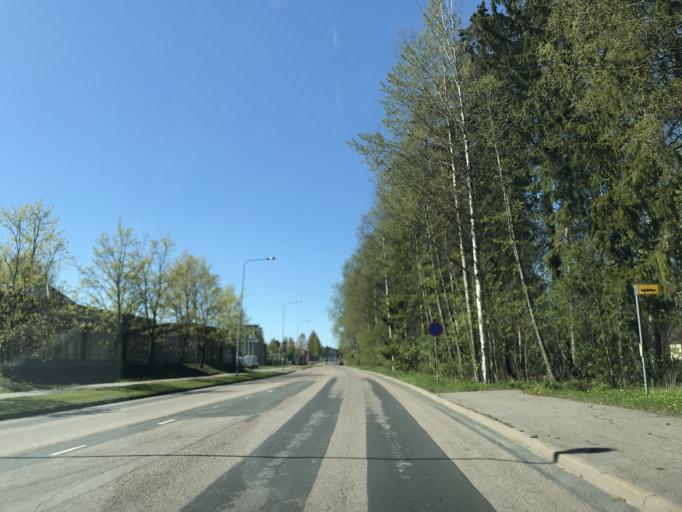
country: FI
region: Uusimaa
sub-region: Helsinki
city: Hyvinge
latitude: 60.6264
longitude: 24.8685
